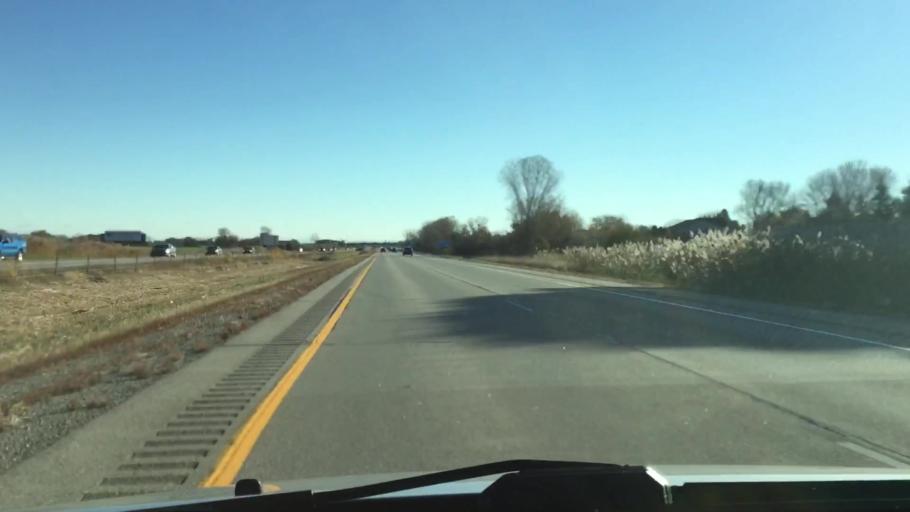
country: US
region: Wisconsin
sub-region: Outagamie County
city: Appleton
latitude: 44.2982
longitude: -88.3916
